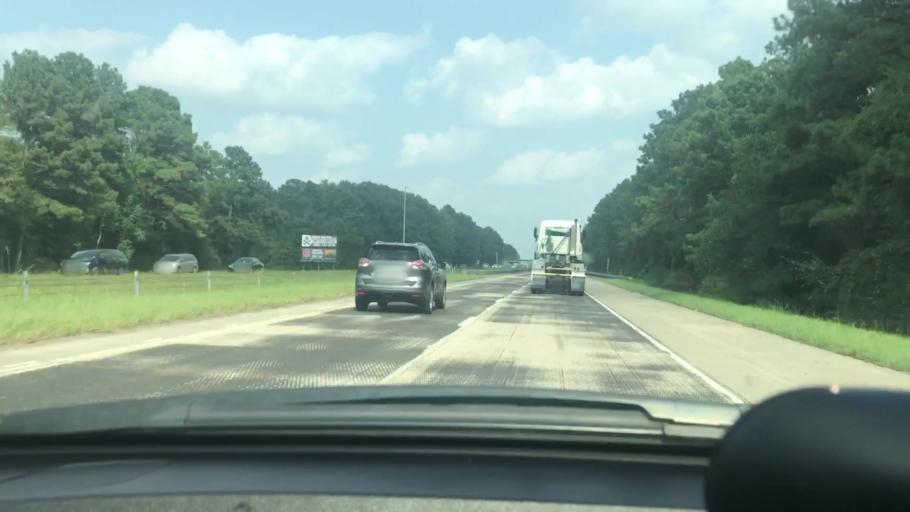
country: US
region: Louisiana
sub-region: Tangipahoa Parish
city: Hammond
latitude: 30.4794
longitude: -90.5086
